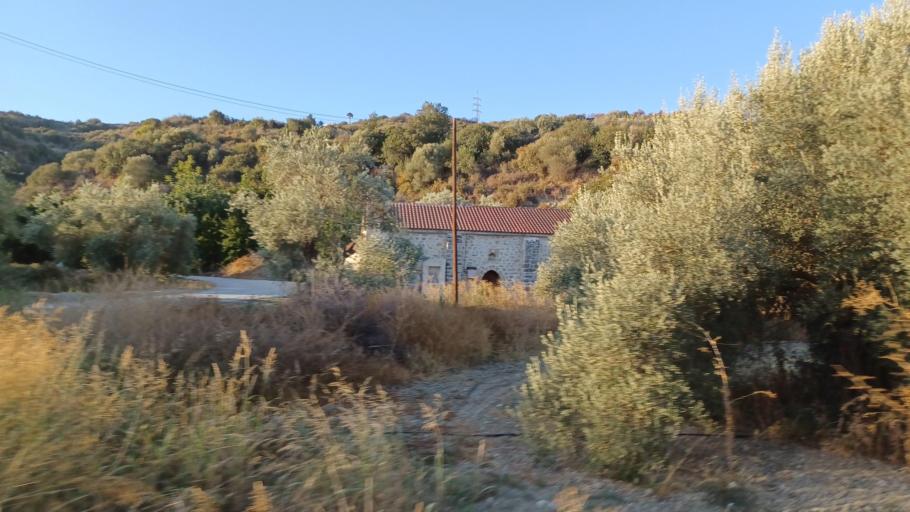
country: CY
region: Pafos
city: Polis
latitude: 34.9775
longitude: 32.4615
